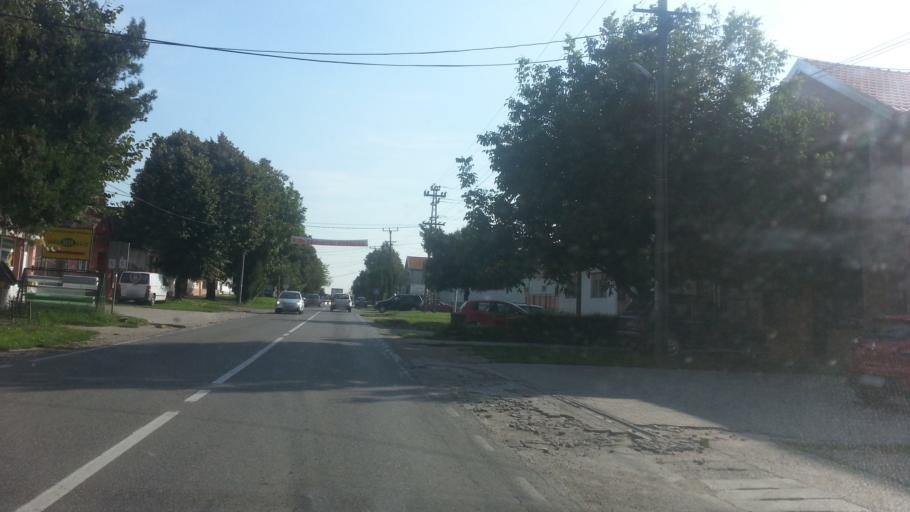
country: RS
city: Novi Banovci
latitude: 44.9603
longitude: 20.2810
